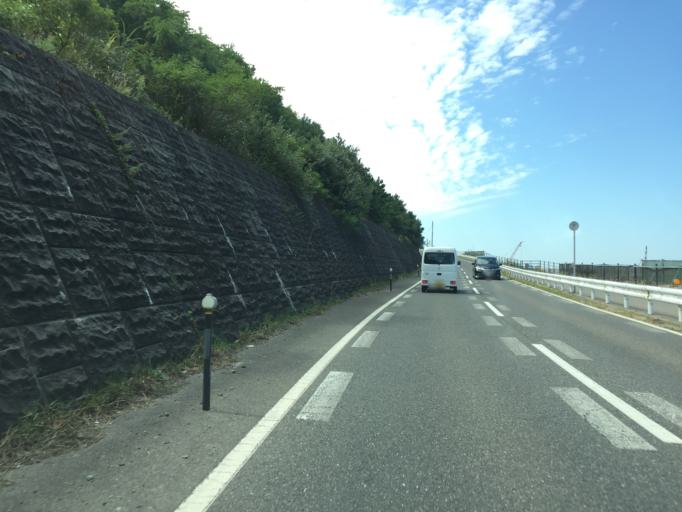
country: JP
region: Niigata
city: Niigata-shi
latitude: 37.9313
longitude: 139.0392
